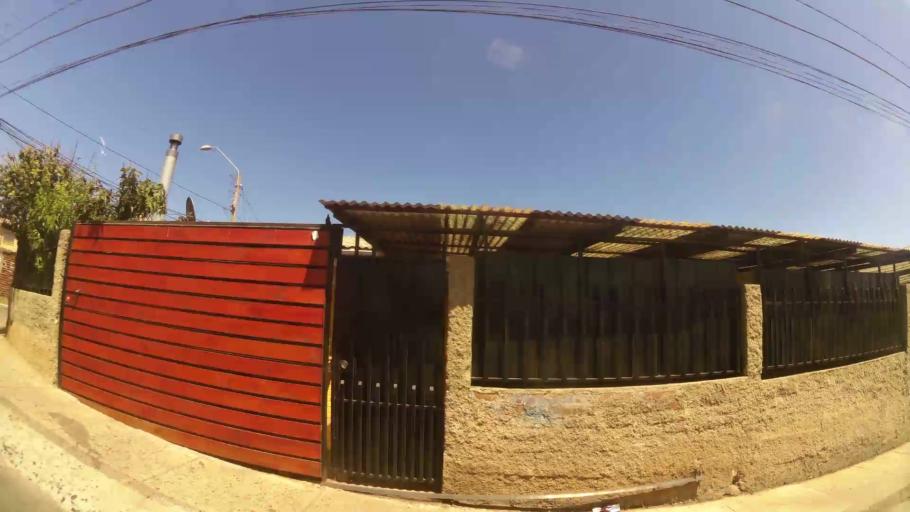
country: CL
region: Valparaiso
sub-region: Provincia de Valparaiso
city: Valparaiso
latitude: -33.0322
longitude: -71.6529
